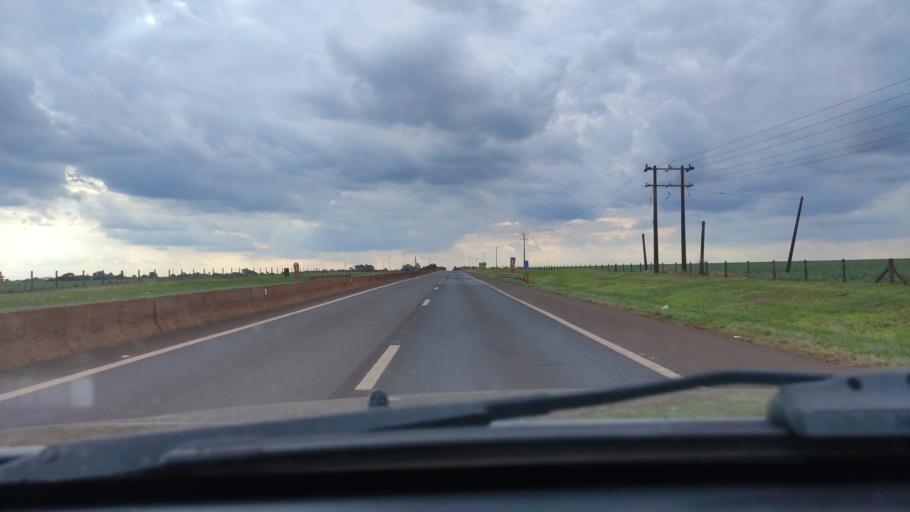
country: BR
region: Sao Paulo
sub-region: Palmital
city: Palmital
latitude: -22.8192
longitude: -50.0468
